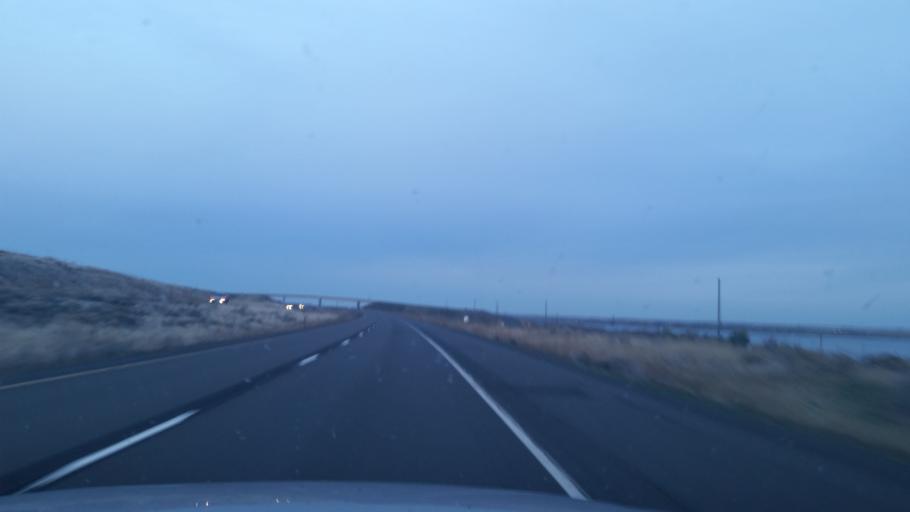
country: US
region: Washington
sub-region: Adams County
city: Ritzville
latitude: 47.2561
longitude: -118.0867
